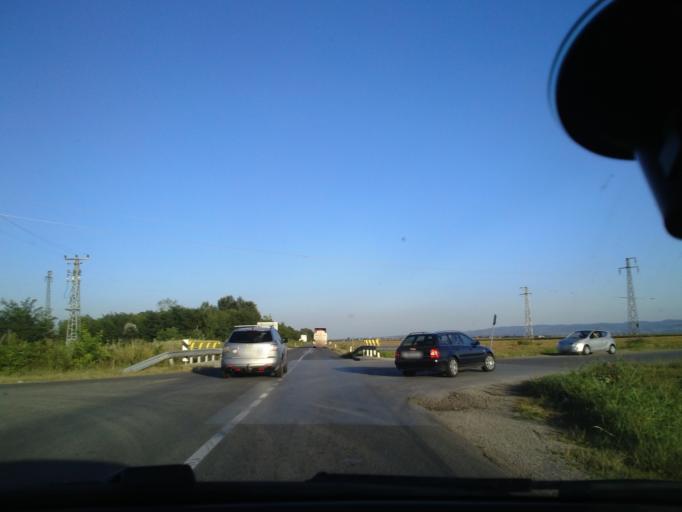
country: RS
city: Kisac
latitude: 45.3197
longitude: 19.7068
